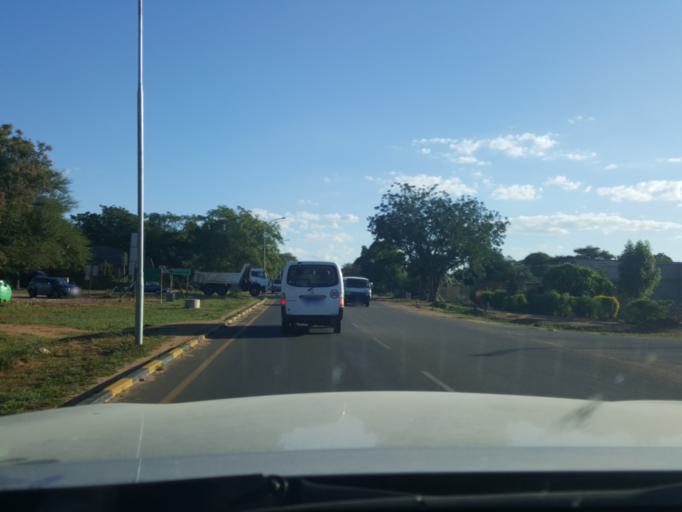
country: BW
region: South East
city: Gaborone
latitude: -24.6417
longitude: 25.9391
